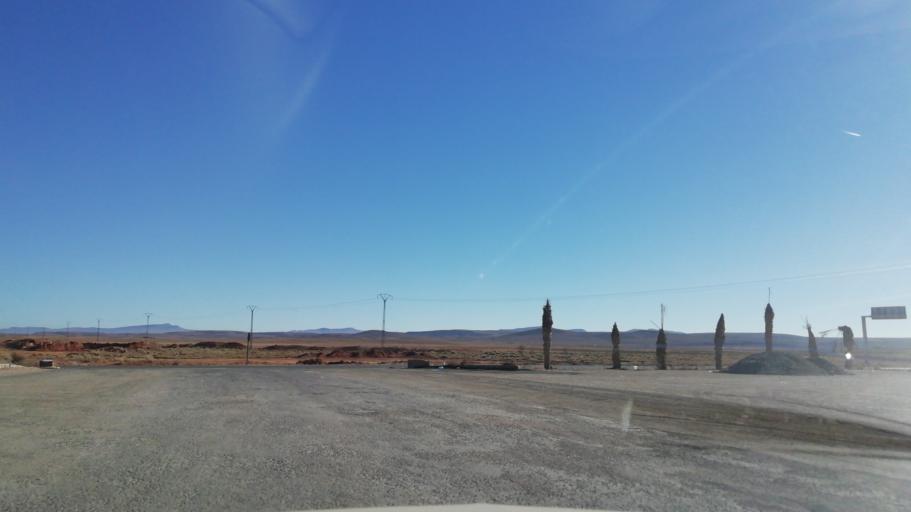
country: DZ
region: El Bayadh
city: El Bayadh
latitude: 33.6551
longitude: 0.9075
